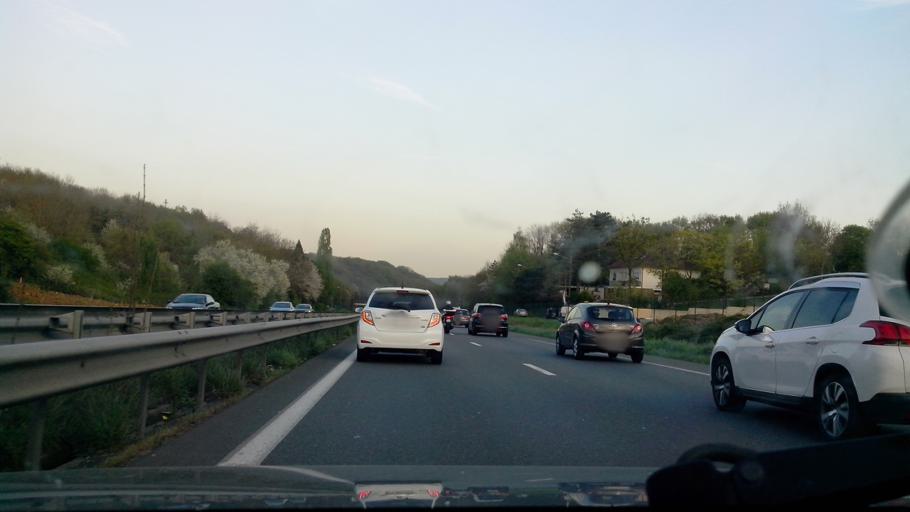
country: FR
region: Ile-de-France
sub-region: Departement de l'Essonne
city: Bures-sur-Yvette
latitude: 48.7143
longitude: 2.1759
